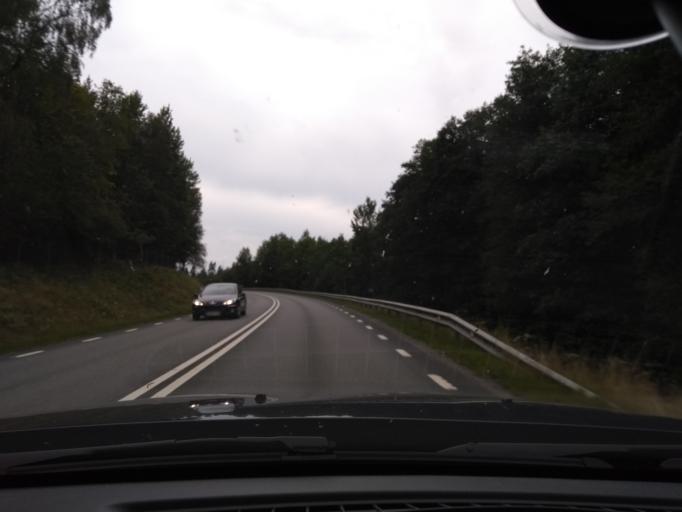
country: SE
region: Joenkoeping
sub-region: Eksjo Kommun
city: Eksjoe
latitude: 57.6390
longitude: 14.8453
